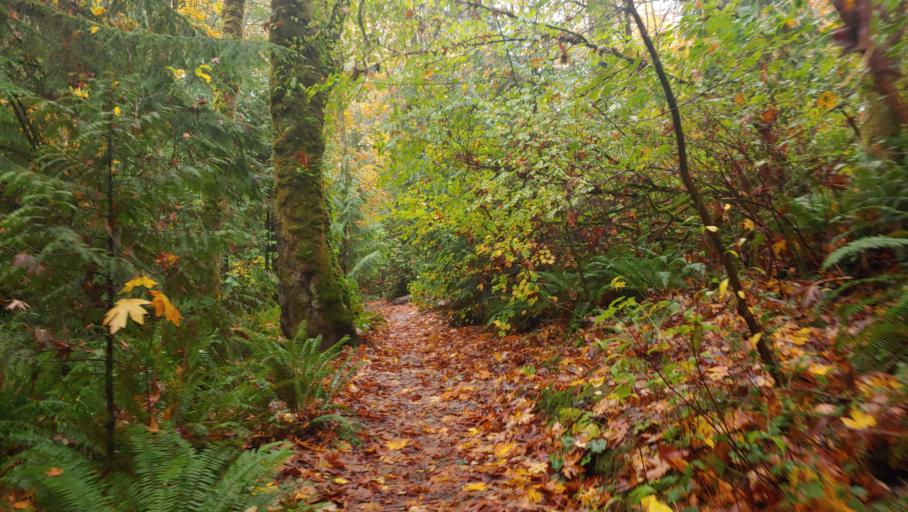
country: US
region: Washington
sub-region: King County
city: Bryn Mawr-Skyway
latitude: 47.5046
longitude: -122.2469
